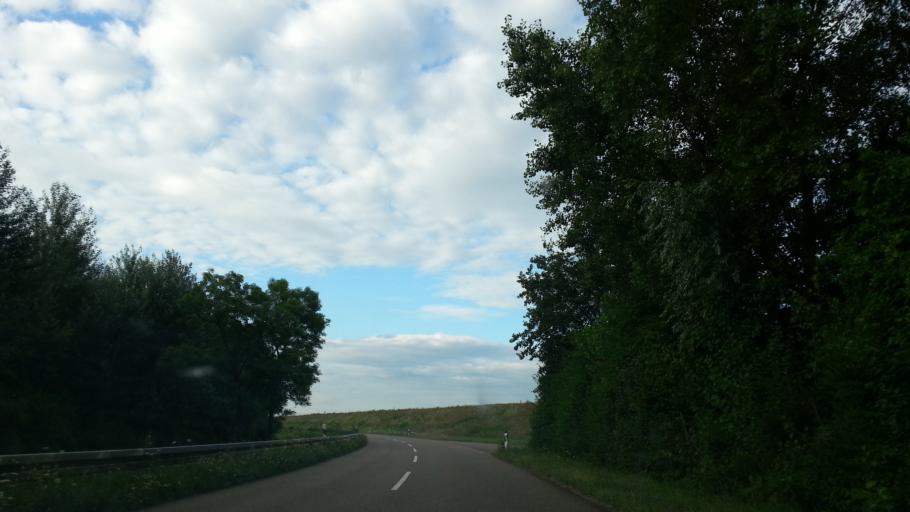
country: DE
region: Baden-Wuerttemberg
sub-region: Freiburg Region
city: Schwanau
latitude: 48.3646
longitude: 7.7382
